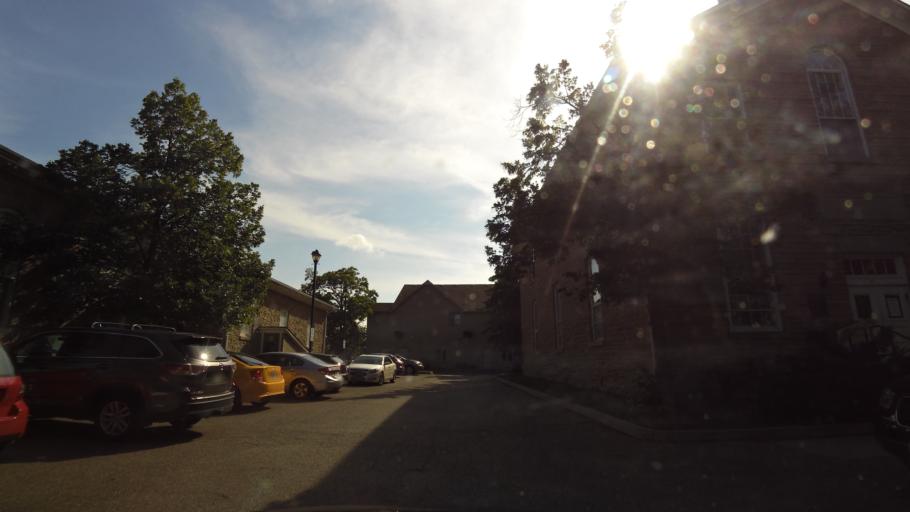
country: CA
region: Ontario
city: Burlington
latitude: 43.3349
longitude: -79.8926
